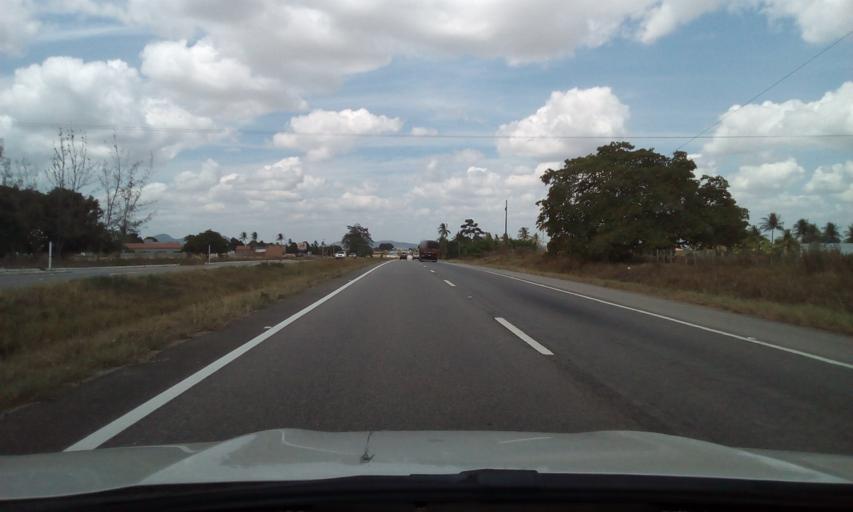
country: BR
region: Paraiba
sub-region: Pilar
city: Pilar
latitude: -7.1846
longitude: -35.2967
